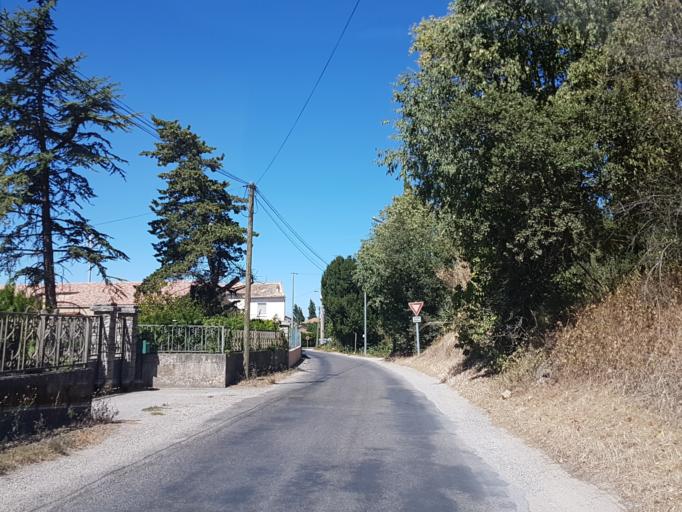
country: FR
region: Provence-Alpes-Cote d'Azur
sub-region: Departement du Vaucluse
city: Orange
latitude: 44.1227
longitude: 4.8020
